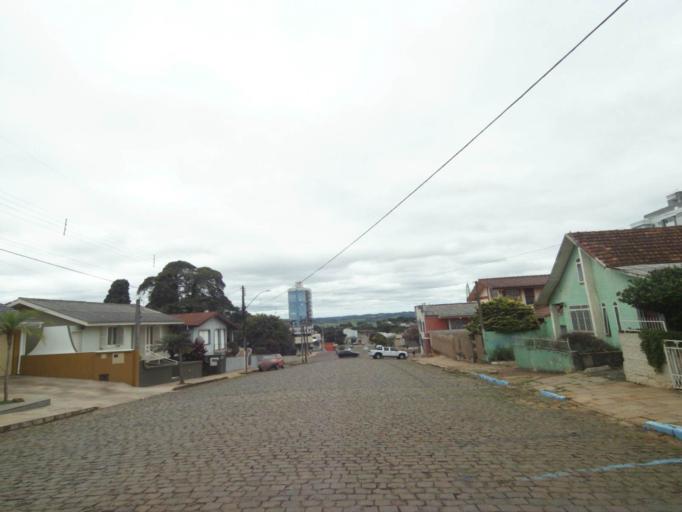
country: BR
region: Rio Grande do Sul
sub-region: Lagoa Vermelha
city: Lagoa Vermelha
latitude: -28.2108
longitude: -51.5194
